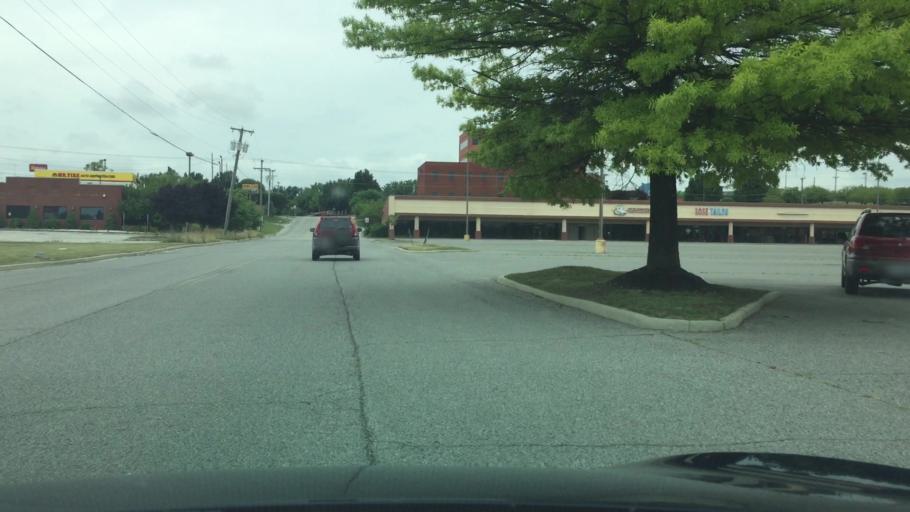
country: US
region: Virginia
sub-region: Montgomery County
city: Merrimac
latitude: 37.1668
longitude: -80.4214
